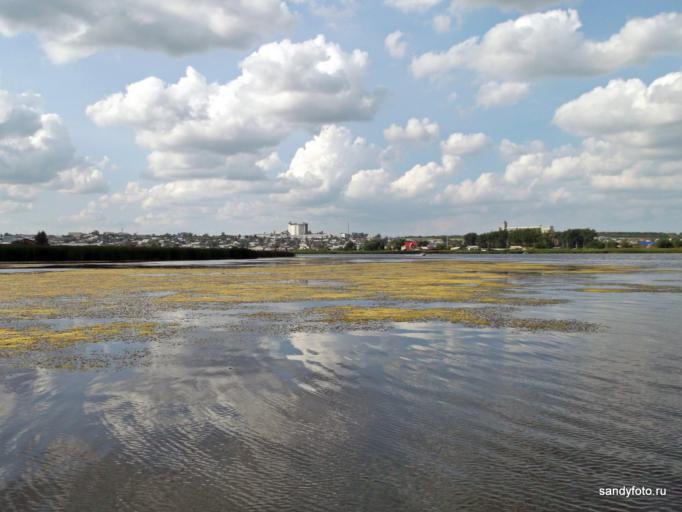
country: RU
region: Chelyabinsk
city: Troitsk
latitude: 54.0845
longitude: 61.5861
